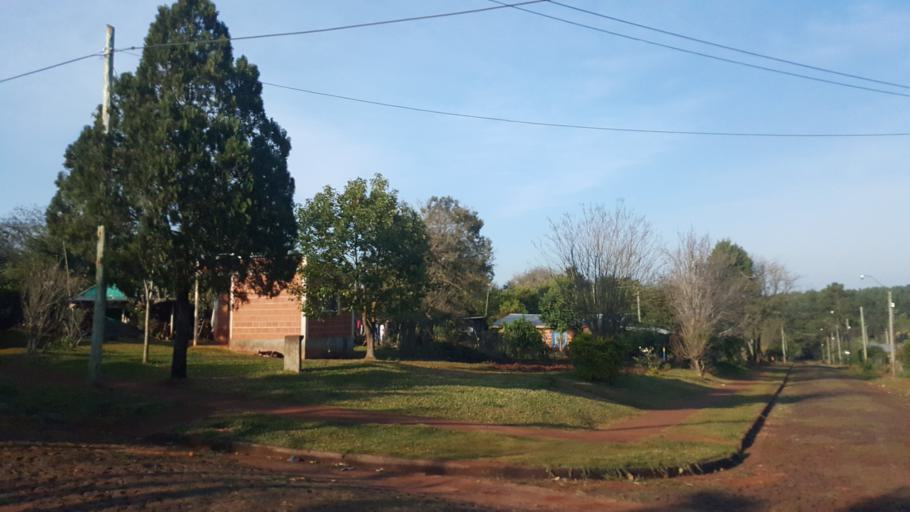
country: AR
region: Misiones
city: Capiovi
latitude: -26.8925
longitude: -55.0728
